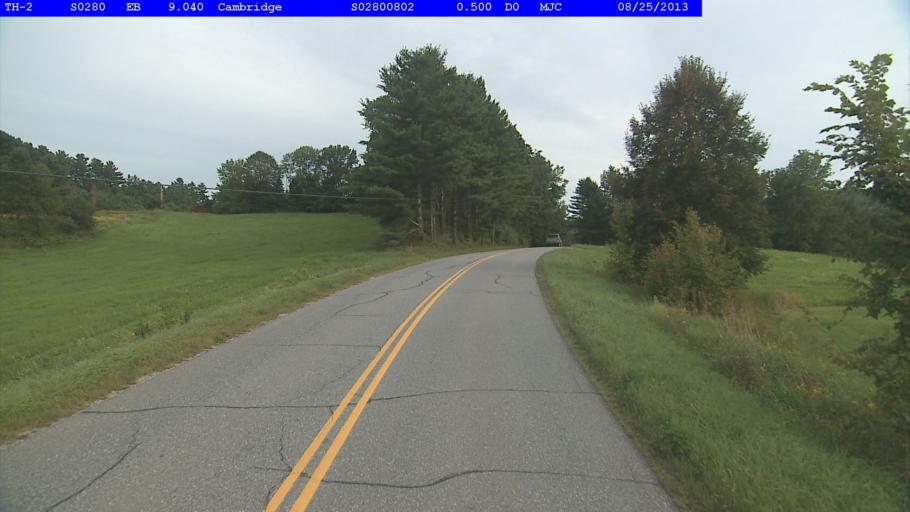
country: US
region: Vermont
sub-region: Chittenden County
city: Jericho
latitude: 44.6563
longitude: -72.8809
